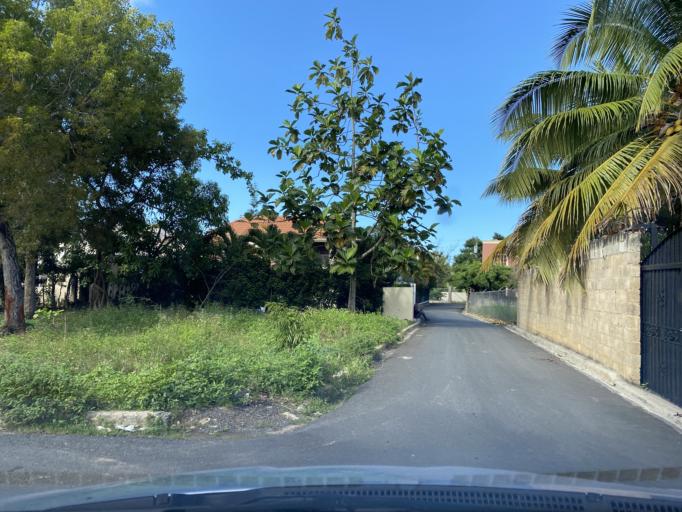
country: DO
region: Samana
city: Las Terrenas
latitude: 19.3055
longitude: -69.5444
